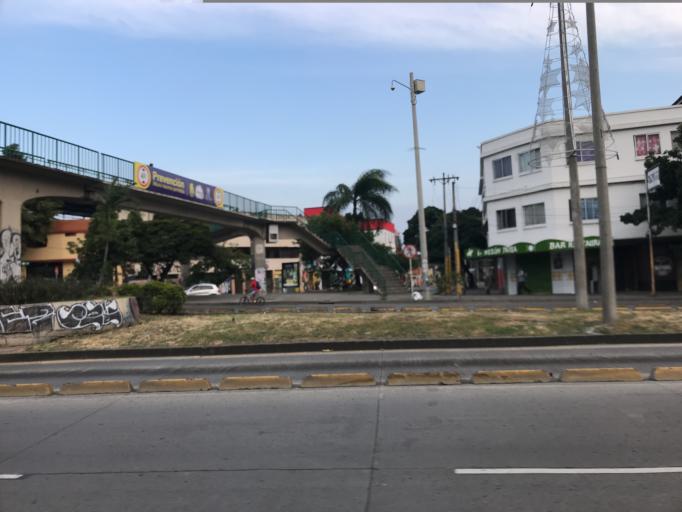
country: CO
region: Valle del Cauca
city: Cali
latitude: 3.4389
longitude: -76.5378
